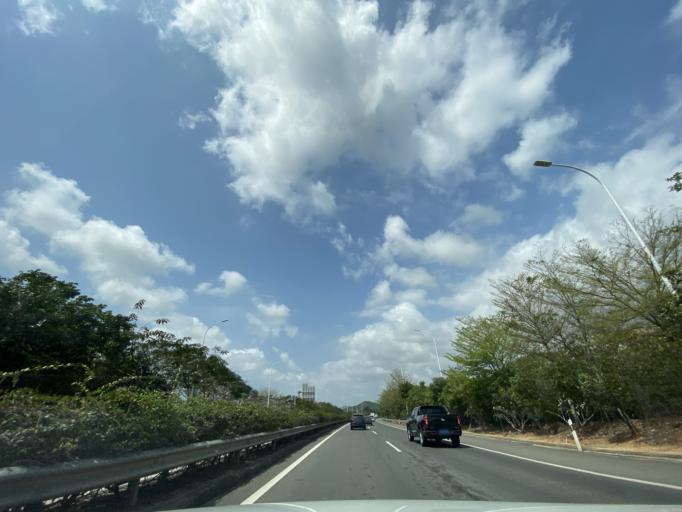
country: CN
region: Hainan
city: Tiandu
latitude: 18.3195
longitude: 109.5714
